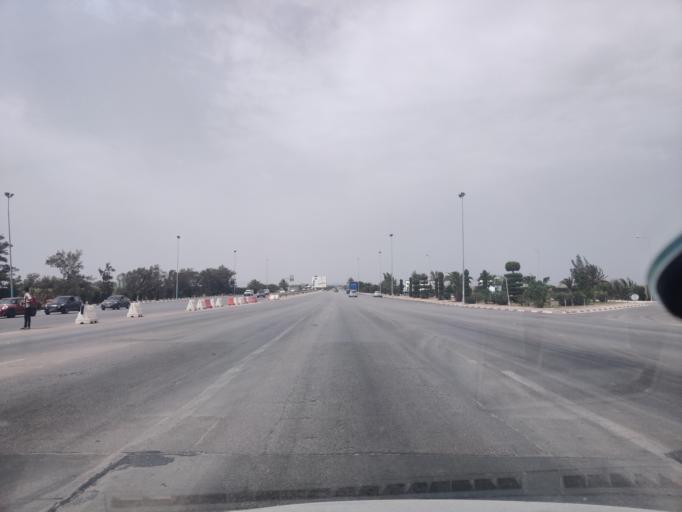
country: TN
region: Susah
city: Sidi Bou Ali
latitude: 36.0039
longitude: 10.4355
